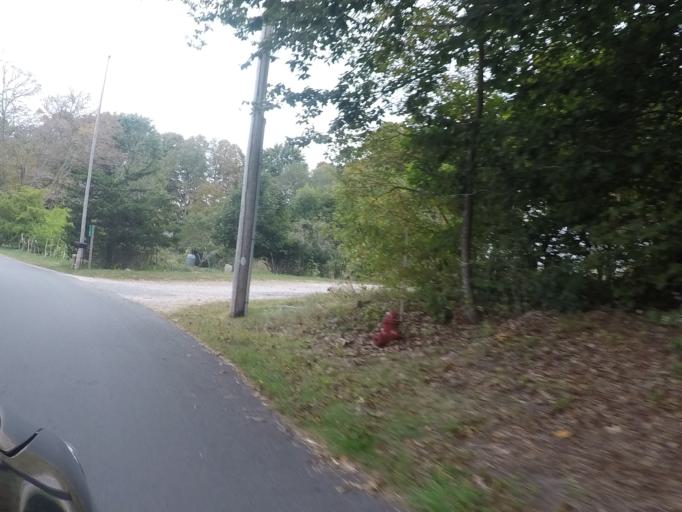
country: US
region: Massachusetts
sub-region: Bristol County
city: Smith Mills
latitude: 41.5736
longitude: -71.0071
